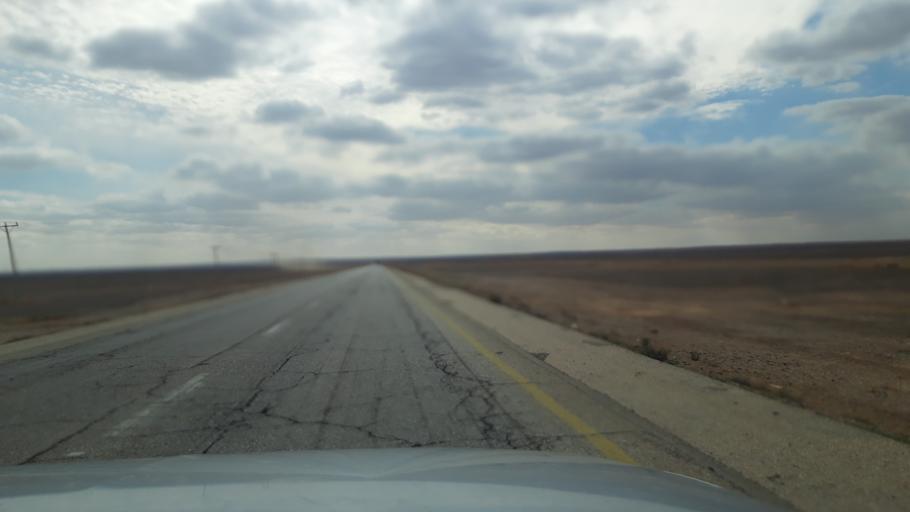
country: JO
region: Amman
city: Al Azraq ash Shamali
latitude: 31.8327
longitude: 36.6276
